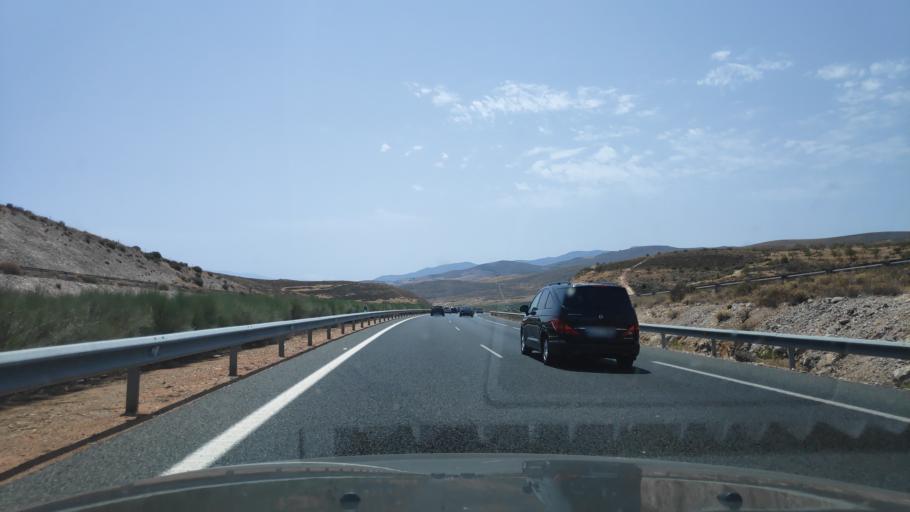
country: ES
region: Andalusia
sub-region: Provincia de Granada
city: Padul
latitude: 36.9999
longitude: -3.6309
